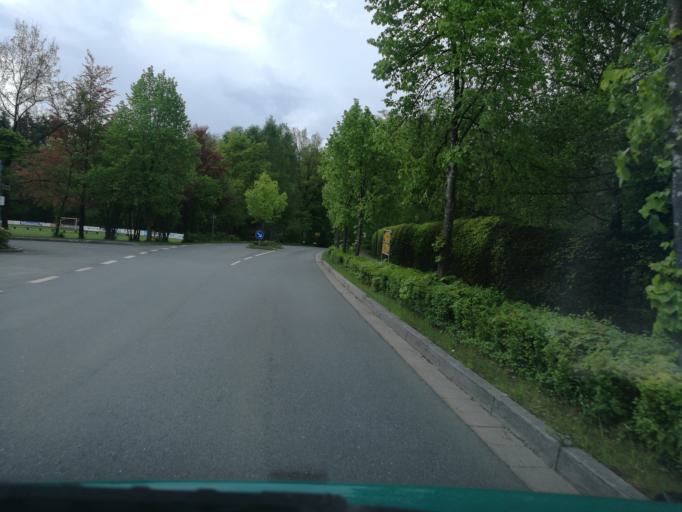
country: DE
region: Bavaria
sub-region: Upper Franconia
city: Sonnefeld
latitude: 50.2060
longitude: 11.1089
